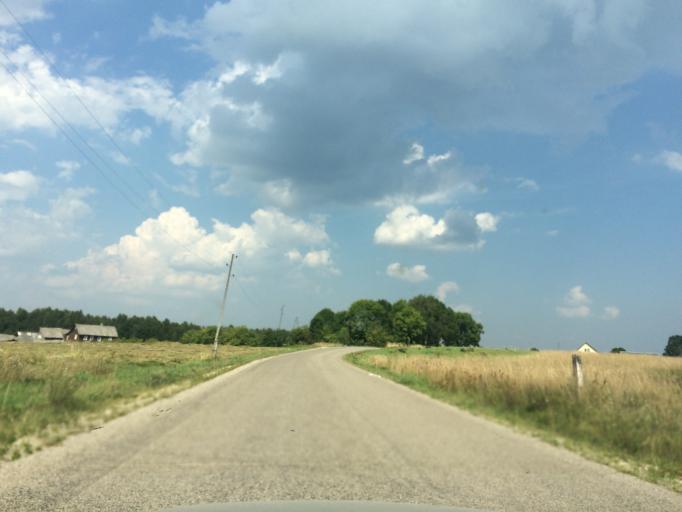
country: LV
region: Rezekne
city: Rezekne
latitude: 56.5513
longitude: 27.3688
